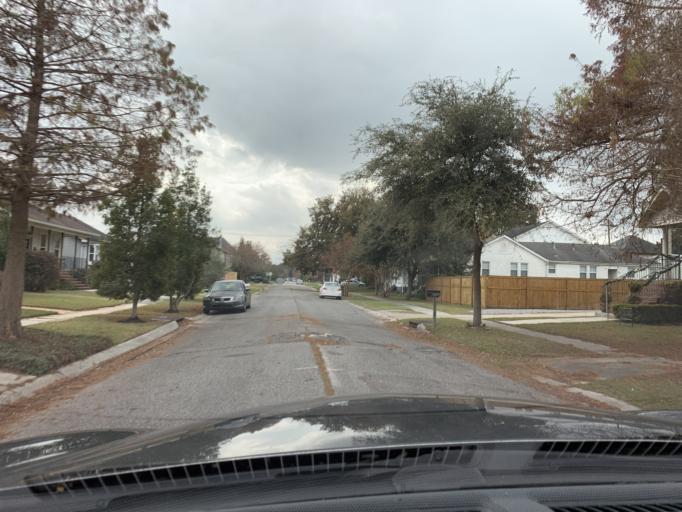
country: US
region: Louisiana
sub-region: Jefferson Parish
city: Metairie
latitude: 30.0130
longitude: -90.1038
